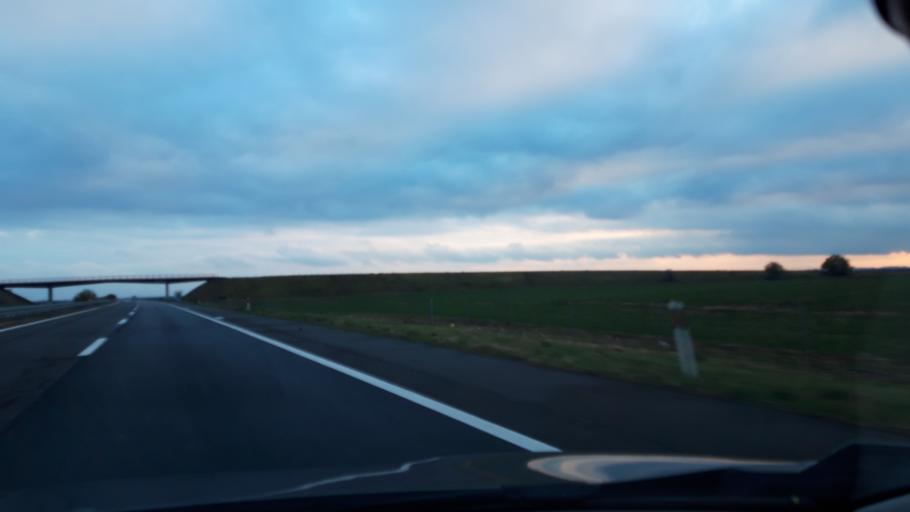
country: RS
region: Autonomna Pokrajina Vojvodina
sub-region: Juznobacki Okrug
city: Vrbas
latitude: 45.6146
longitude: 19.7059
